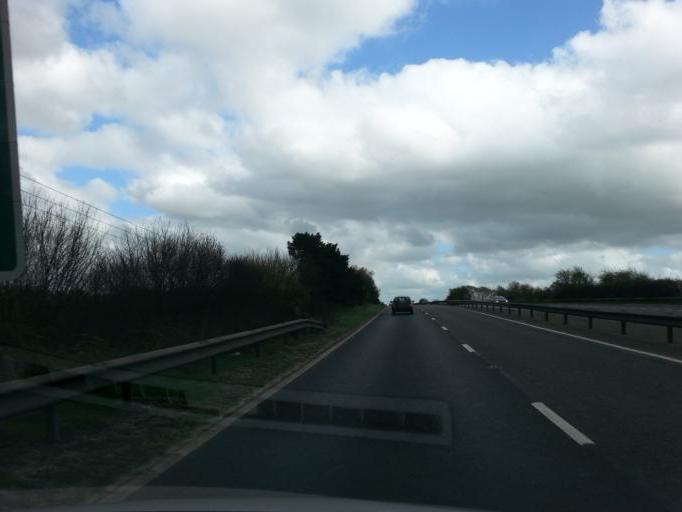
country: GB
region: England
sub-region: Hampshire
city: Kings Worthy
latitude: 51.1773
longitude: -1.3559
